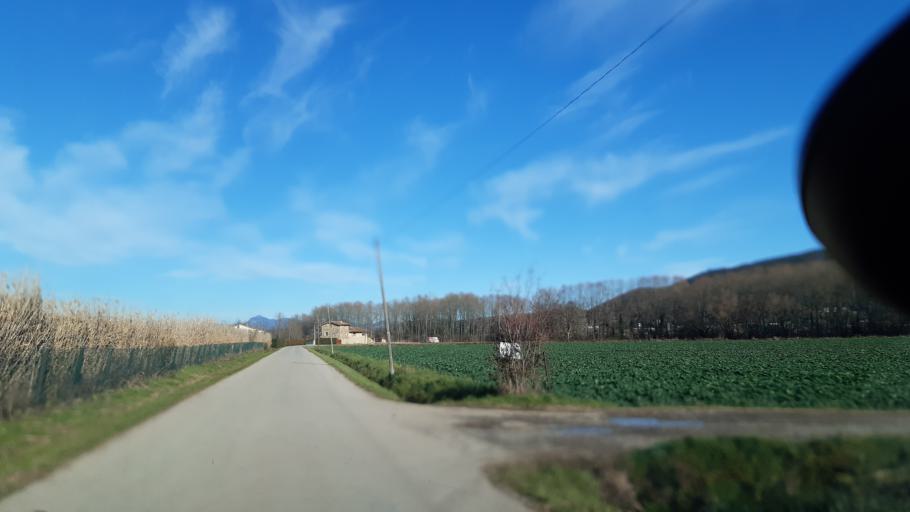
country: ES
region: Catalonia
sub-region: Provincia de Girona
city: Bas
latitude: 42.1413
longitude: 2.4455
